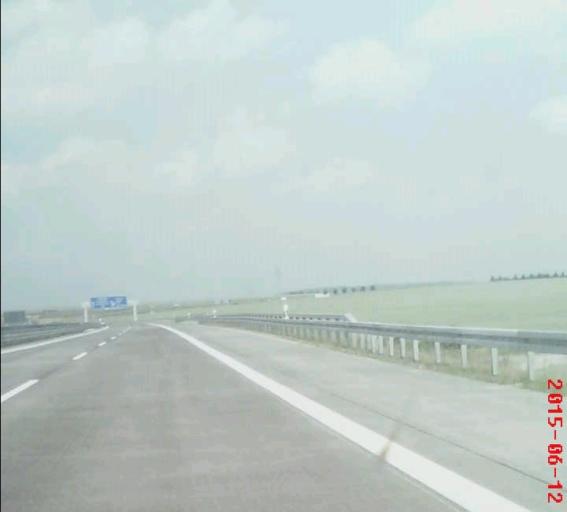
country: DE
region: Saxony-Anhalt
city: Oberroblingen
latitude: 51.4293
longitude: 11.3254
